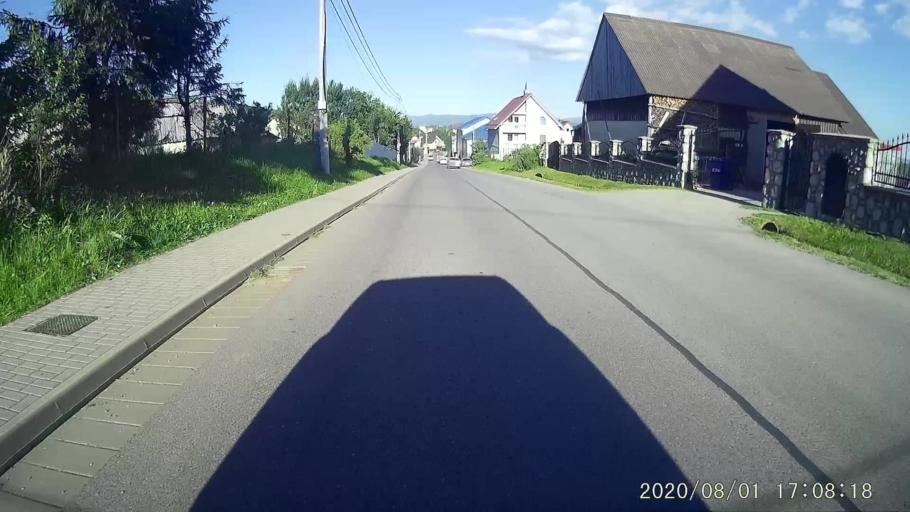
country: SK
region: Presovsky
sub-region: Okres Poprad
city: Zdiar
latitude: 49.2335
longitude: 20.3500
